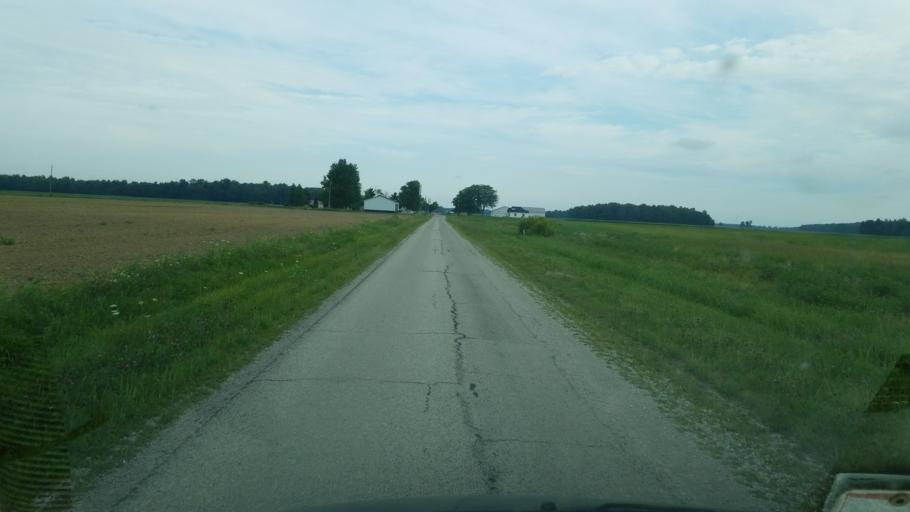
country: US
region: Ohio
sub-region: Crawford County
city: Bucyrus
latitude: 40.9701
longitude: -83.0551
